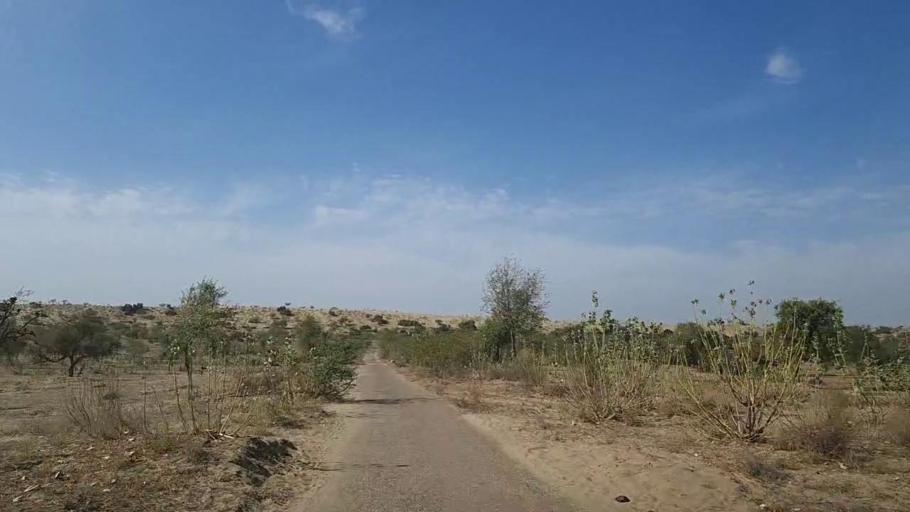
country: PK
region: Sindh
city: Naukot
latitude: 24.8321
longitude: 69.5480
